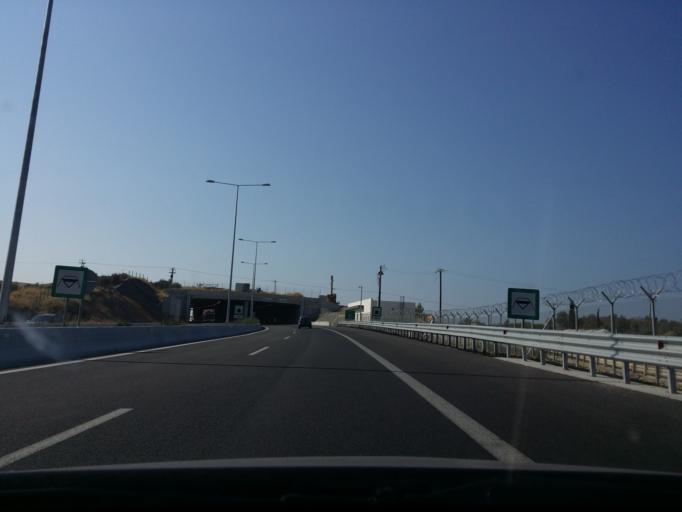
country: GR
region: Peloponnese
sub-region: Nomos Korinthias
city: Xylokastro
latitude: 38.0615
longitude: 22.6562
